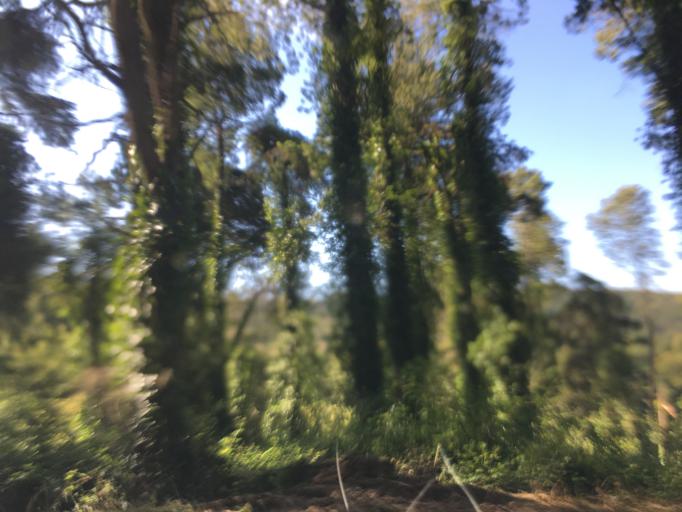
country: PT
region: Lisbon
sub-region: Sintra
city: Colares
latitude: 38.7753
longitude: -9.4602
